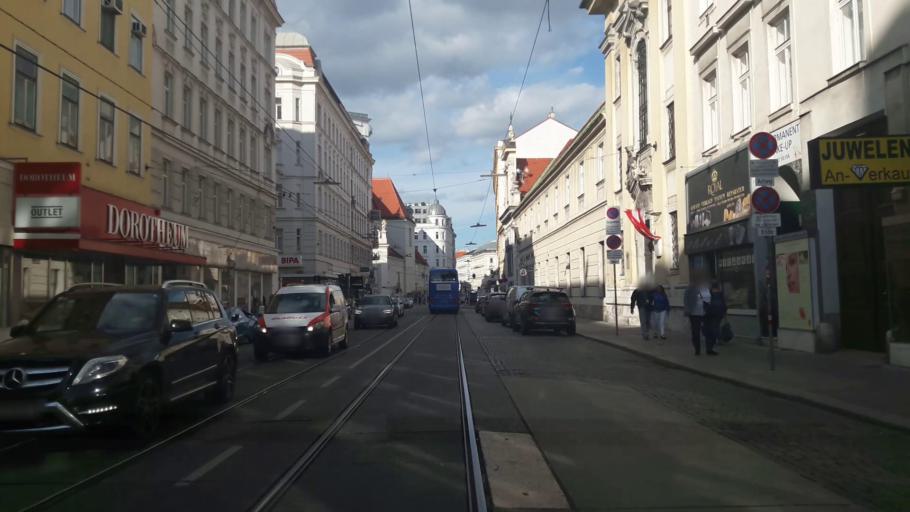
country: AT
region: Vienna
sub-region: Wien Stadt
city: Vienna
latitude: 48.2145
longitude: 16.3800
